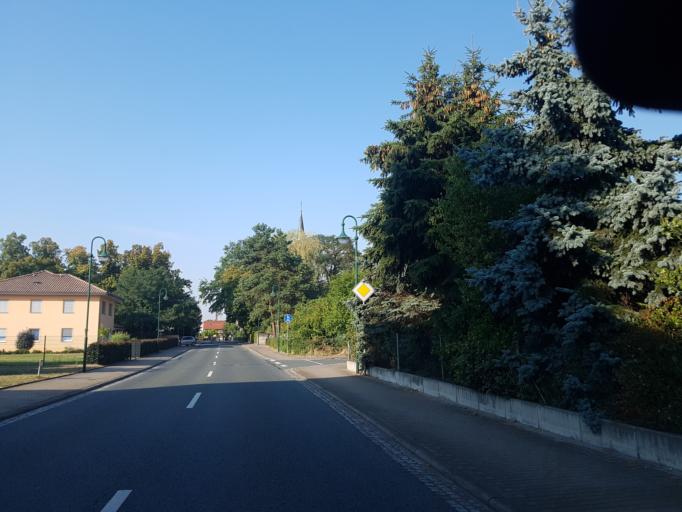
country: DE
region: Saxony
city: Nauwalde
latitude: 51.4140
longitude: 13.4496
